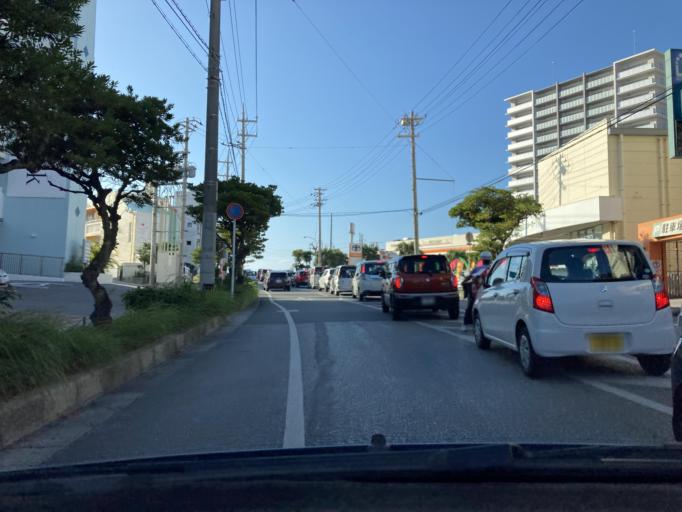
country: JP
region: Okinawa
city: Ginowan
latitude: 26.2585
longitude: 127.7122
